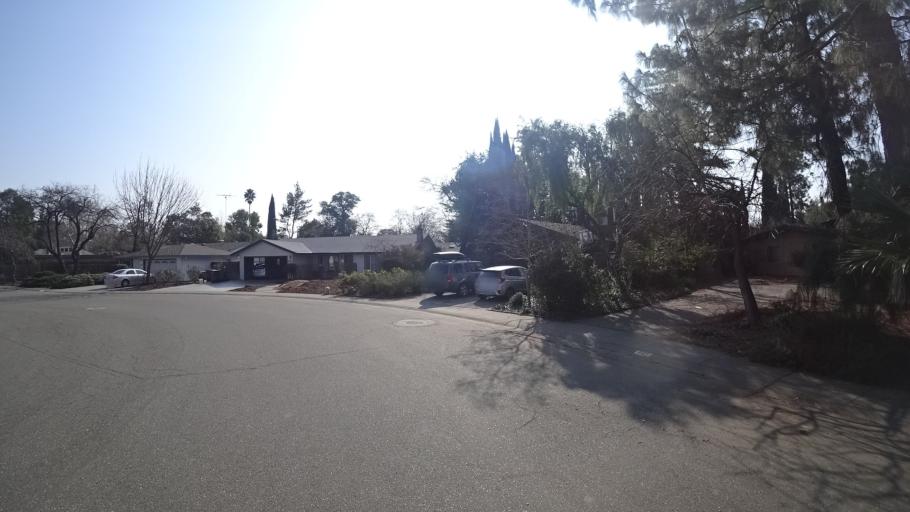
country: US
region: California
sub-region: Yolo County
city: Davis
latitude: 38.5507
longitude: -121.7714
